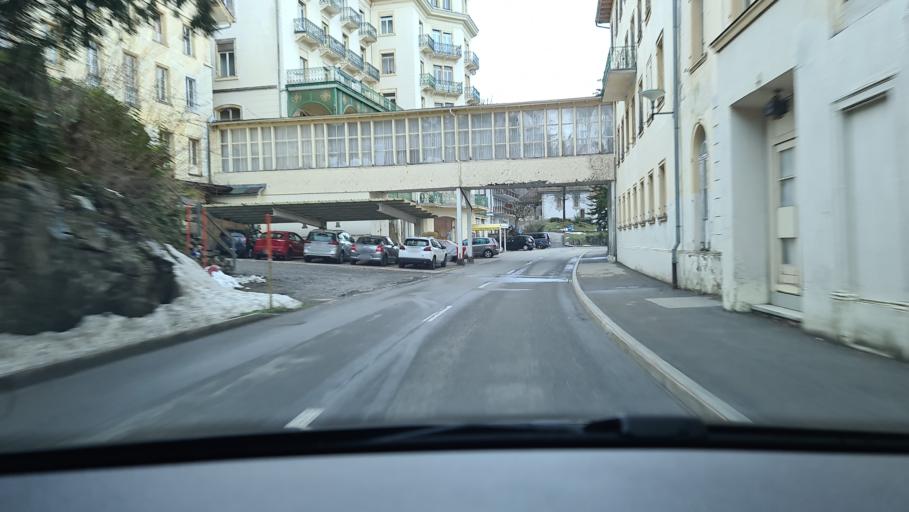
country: CH
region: Uri
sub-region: Uri
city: Bauen
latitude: 46.9696
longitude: 8.5861
